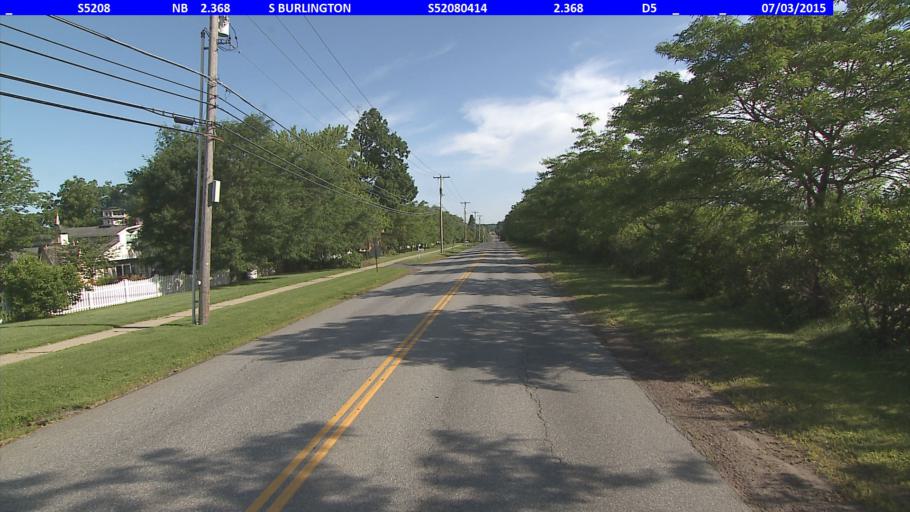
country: US
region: Vermont
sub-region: Chittenden County
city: South Burlington
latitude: 44.4445
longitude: -73.1773
